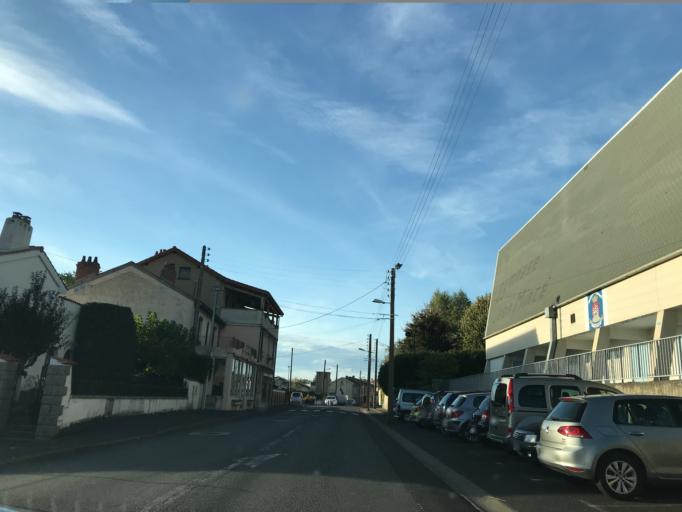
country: FR
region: Auvergne
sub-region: Departement du Puy-de-Dome
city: Thiers
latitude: 45.8606
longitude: 3.5367
